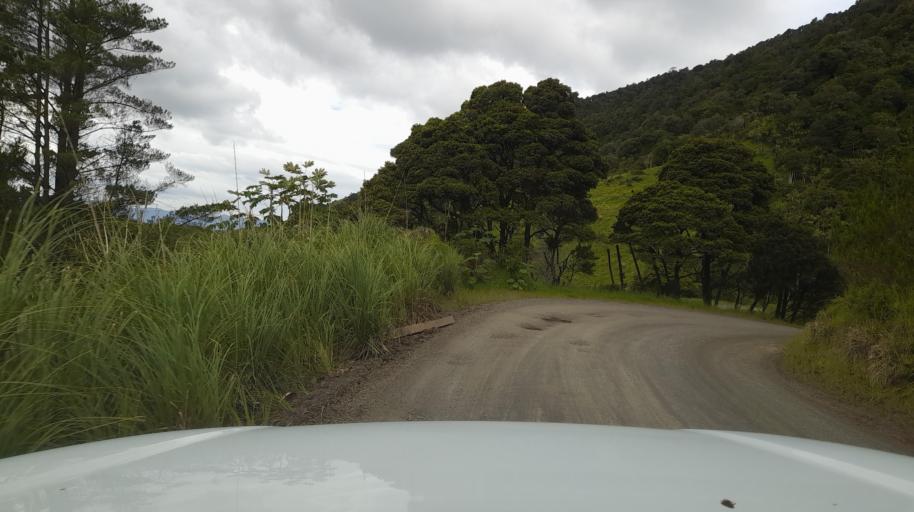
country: NZ
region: Northland
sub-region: Far North District
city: Kaitaia
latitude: -35.3438
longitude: 173.3694
